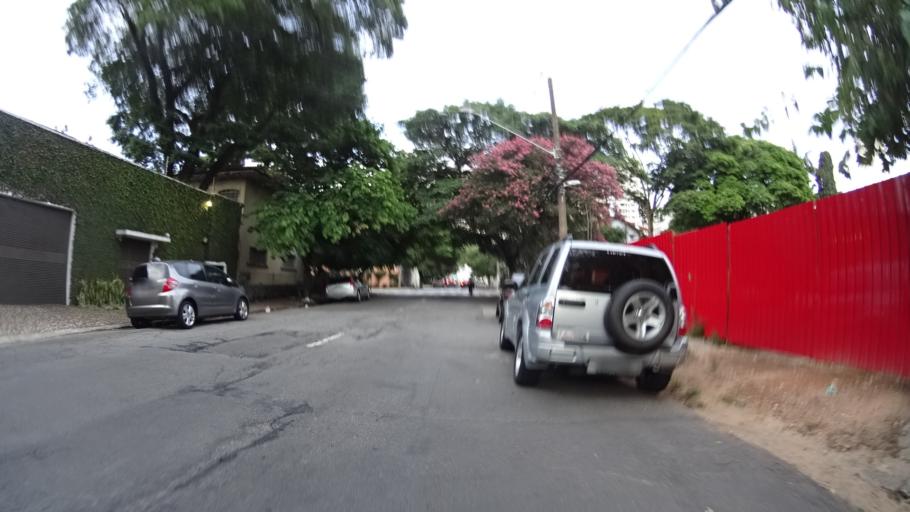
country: BR
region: Sao Paulo
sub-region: Sao Paulo
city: Sao Paulo
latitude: -23.5750
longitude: -46.6615
